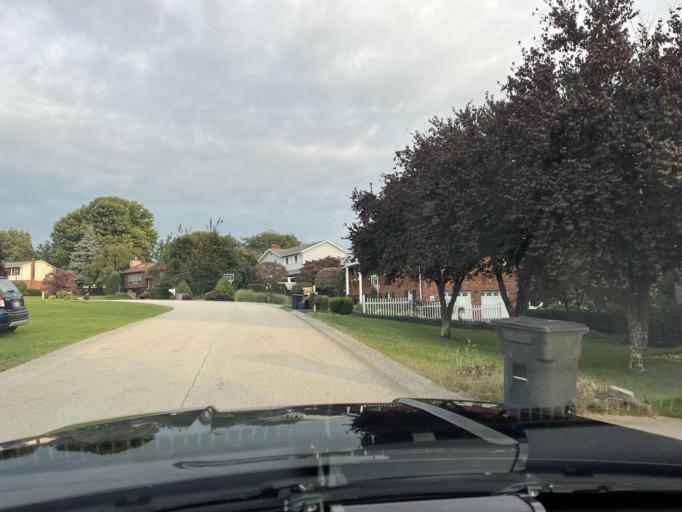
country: US
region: Pennsylvania
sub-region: Fayette County
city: South Uniontown
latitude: 39.8956
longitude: -79.7667
